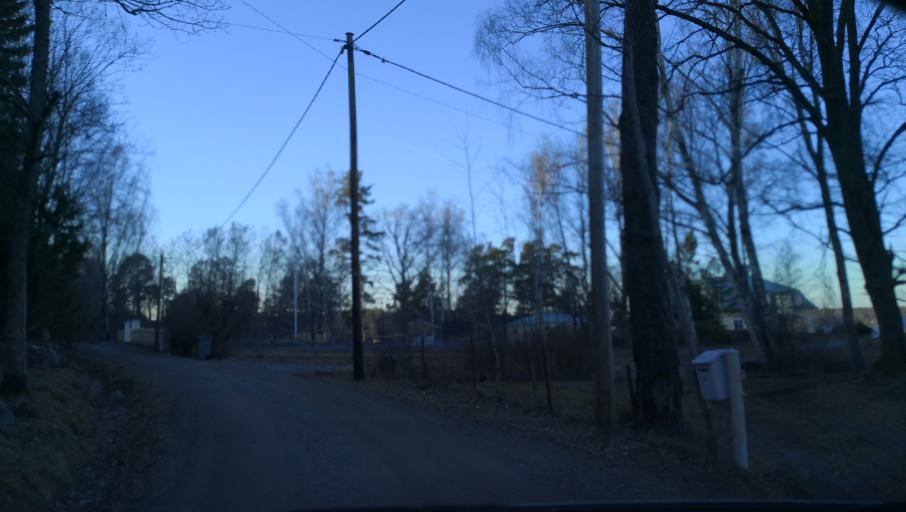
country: SE
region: Stockholm
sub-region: Varmdo Kommun
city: Mortnas
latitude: 59.3335
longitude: 18.4512
